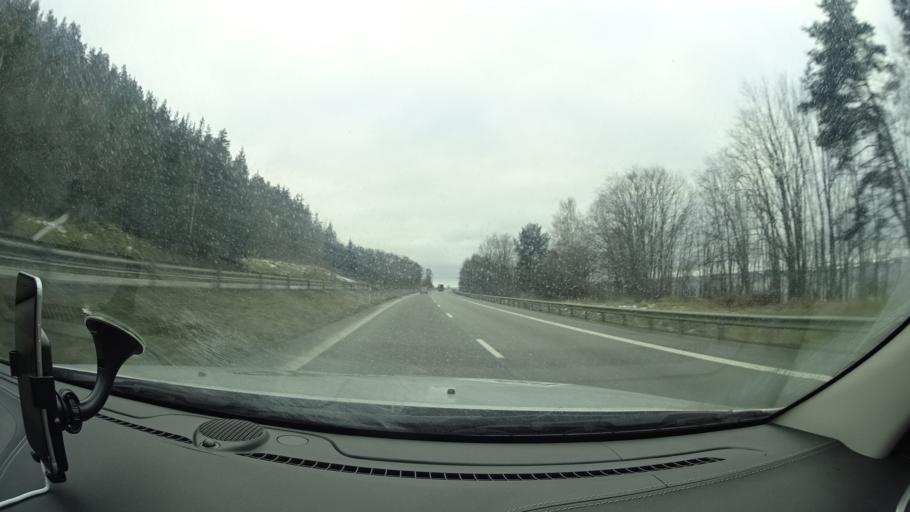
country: SE
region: Joenkoeping
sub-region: Jonkopings Kommun
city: Kaxholmen
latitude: 57.8853
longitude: 14.2827
